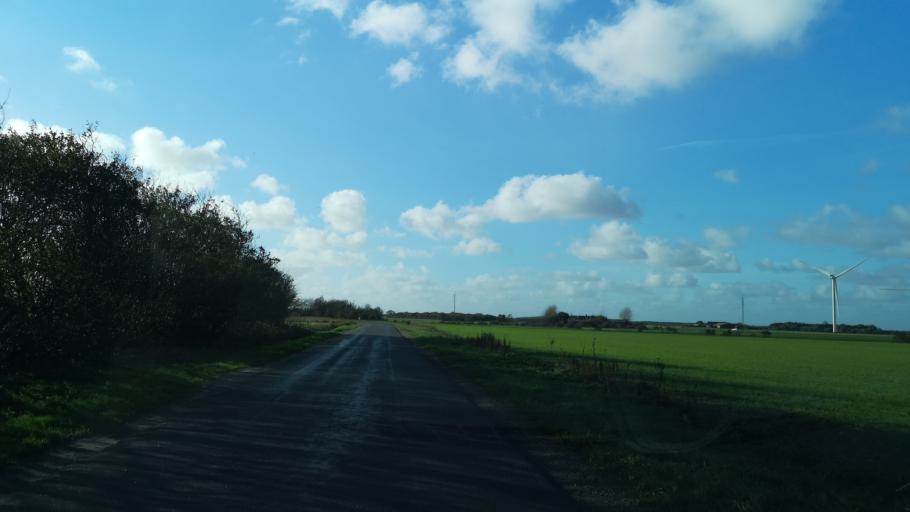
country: DK
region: Central Jutland
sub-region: Ringkobing-Skjern Kommune
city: Skjern
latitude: 55.8379
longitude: 8.3462
